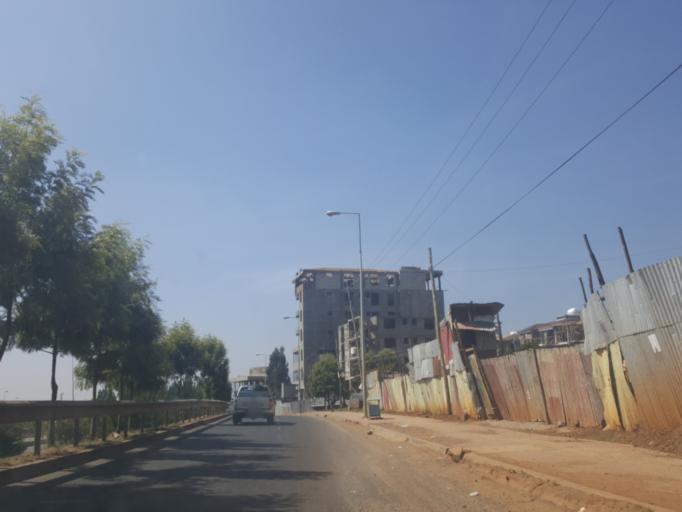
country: ET
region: Adis Abeba
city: Addis Ababa
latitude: 9.0689
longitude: 38.7166
